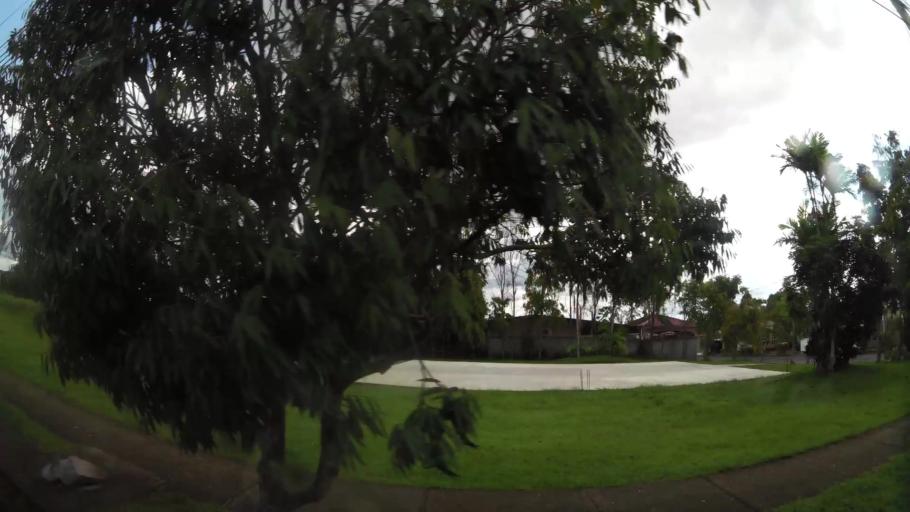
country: PA
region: Panama
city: Nuevo Arraijan
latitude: 8.9371
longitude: -79.7399
